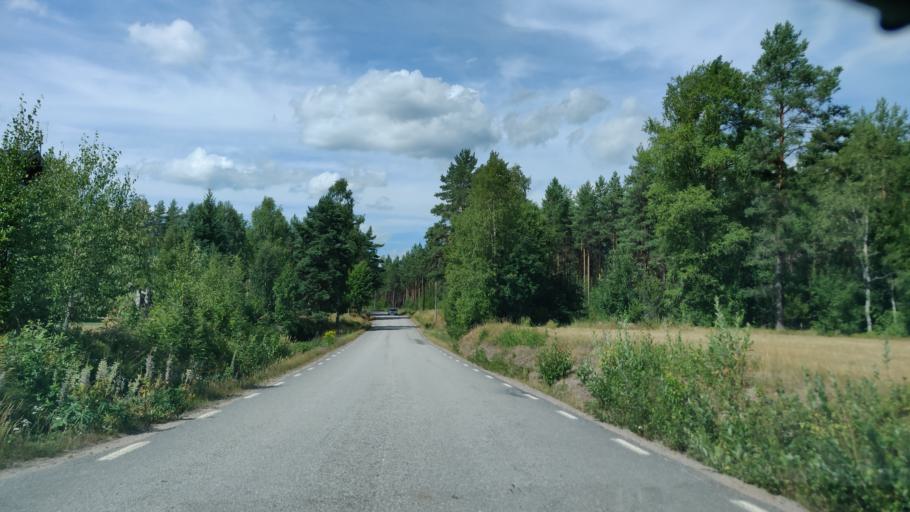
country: SE
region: Vaermland
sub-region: Hagfors Kommun
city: Ekshaerad
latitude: 60.0710
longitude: 13.5358
